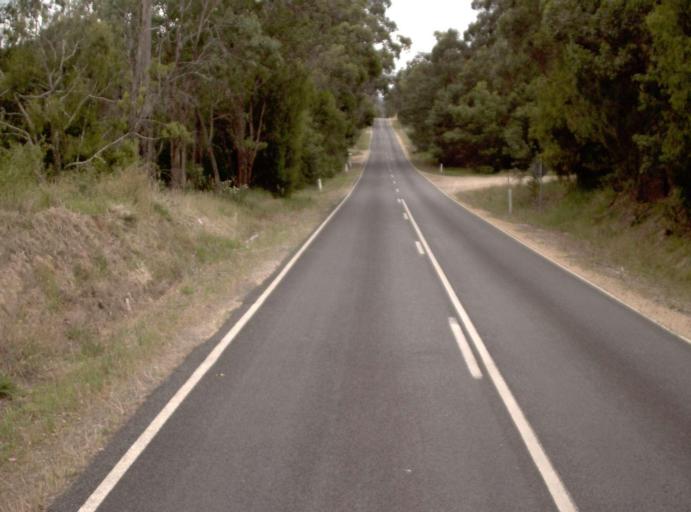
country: AU
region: Victoria
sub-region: East Gippsland
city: Bairnsdale
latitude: -37.7678
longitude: 147.5969
